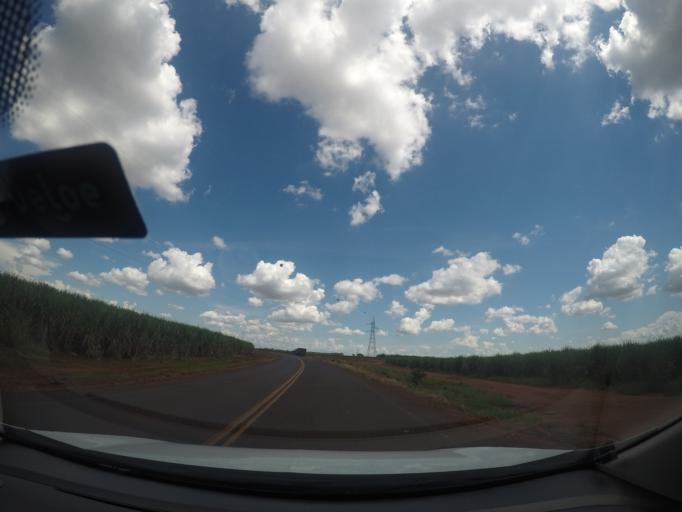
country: BR
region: Minas Gerais
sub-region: Frutal
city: Frutal
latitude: -19.8459
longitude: -48.7380
